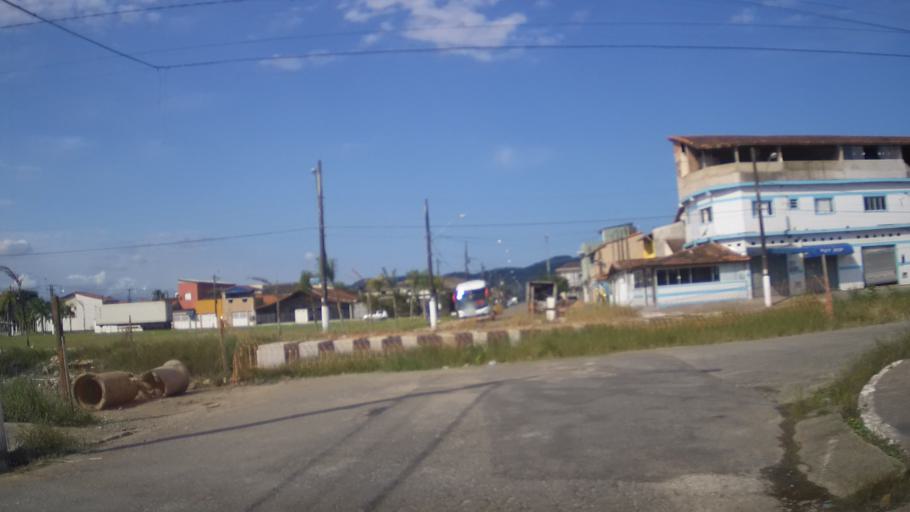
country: BR
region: Sao Paulo
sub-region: Praia Grande
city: Praia Grande
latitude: -23.9979
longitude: -46.4274
